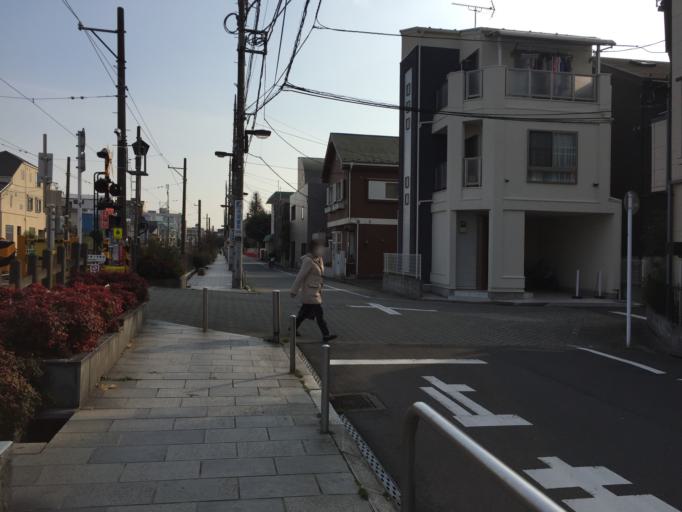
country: JP
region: Tokyo
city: Tokyo
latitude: 35.6626
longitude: 139.6420
